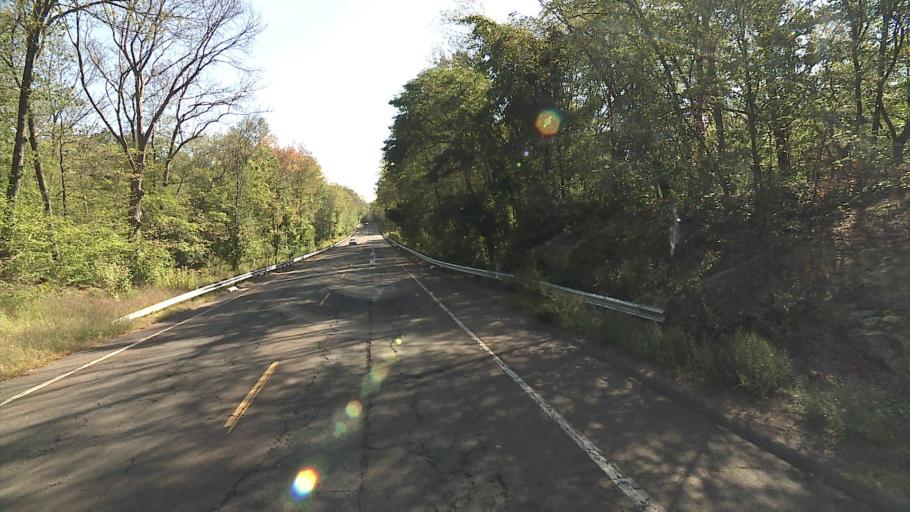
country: US
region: Connecticut
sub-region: Middlesex County
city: Higganum
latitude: 41.5134
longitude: -72.5823
